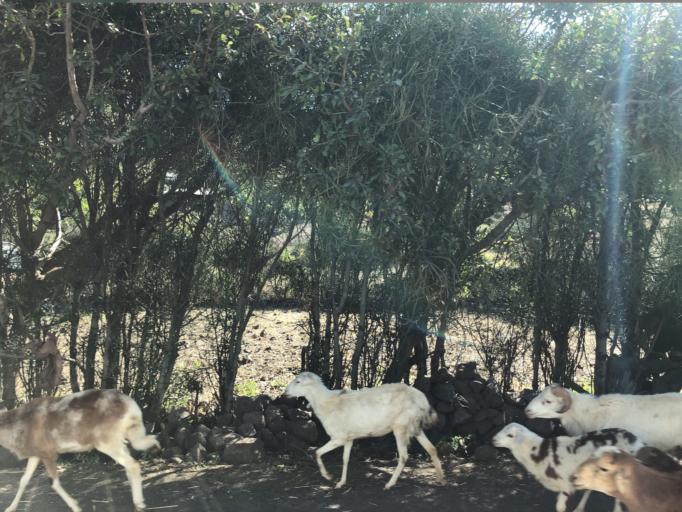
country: ET
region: Amhara
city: Lalibela
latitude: 12.0087
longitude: 39.0506
